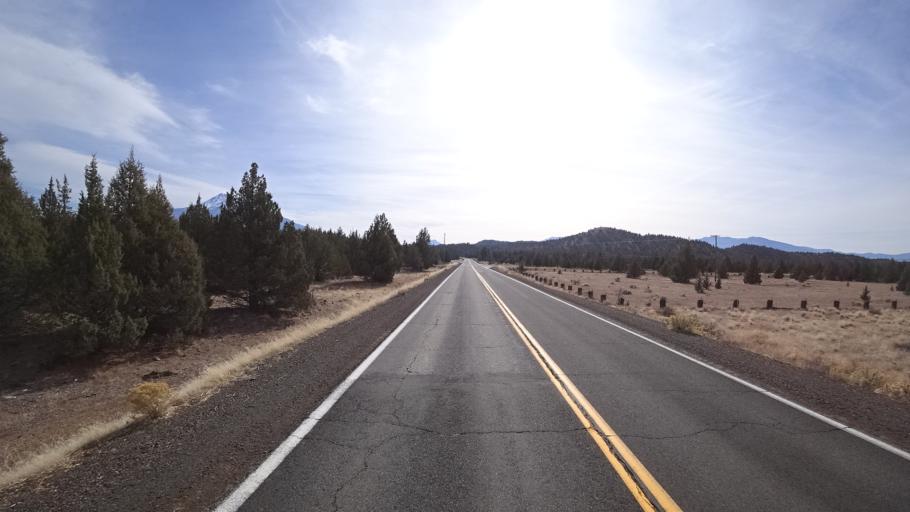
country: US
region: California
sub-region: Siskiyou County
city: Weed
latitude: 41.5856
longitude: -122.3999
